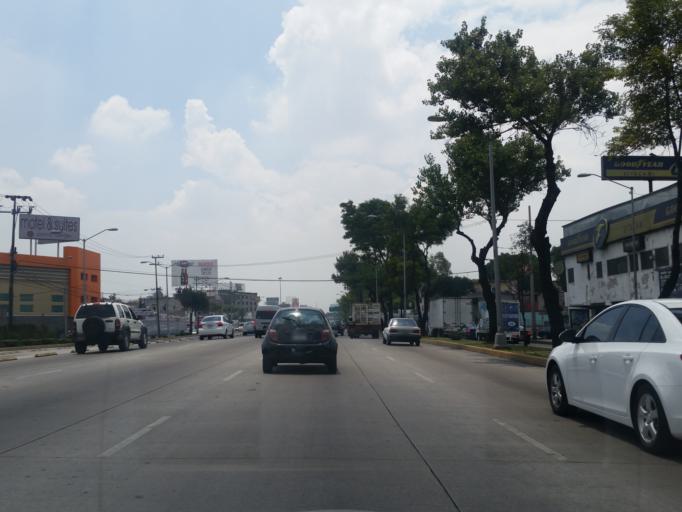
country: MX
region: Mexico
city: Colonia Lindavista
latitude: 19.4771
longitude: -99.1474
